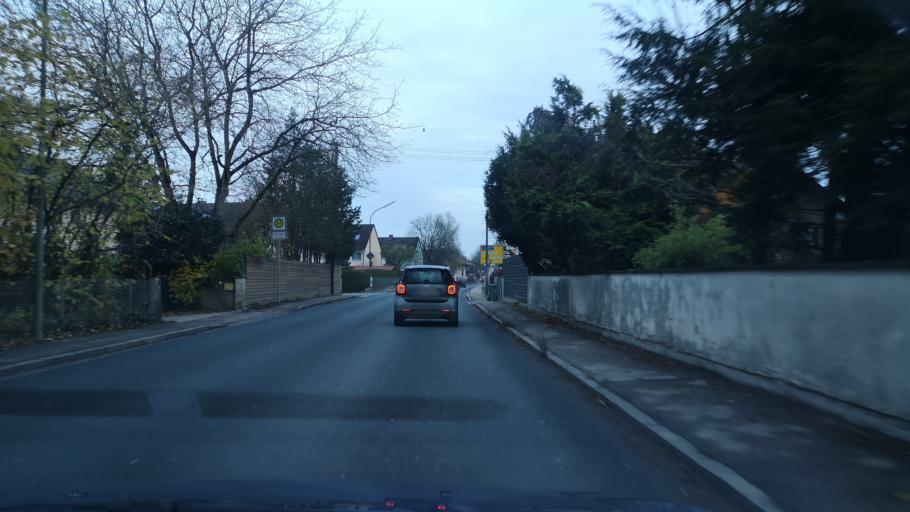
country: DE
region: Bavaria
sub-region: Upper Bavaria
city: Forstinning
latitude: 48.1577
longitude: 11.9012
